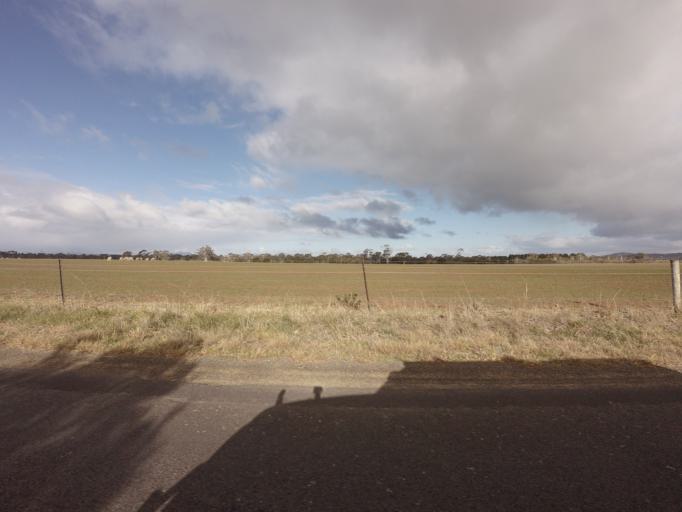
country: AU
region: Tasmania
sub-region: Break O'Day
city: St Helens
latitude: -42.0970
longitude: 148.0681
